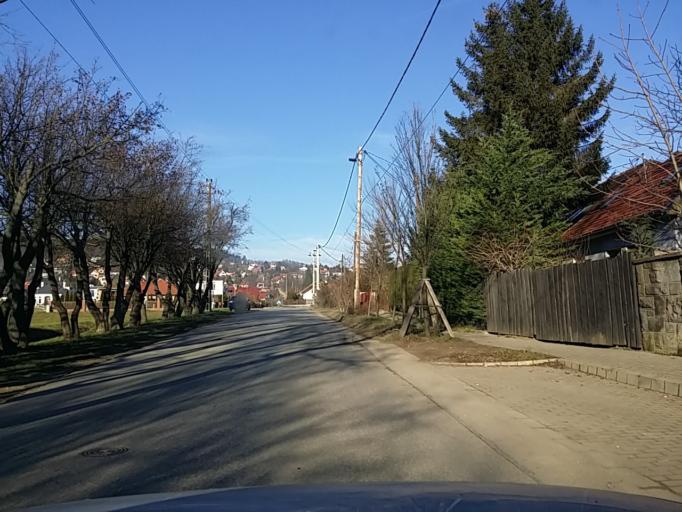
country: HU
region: Pest
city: Pilisszentivan
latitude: 47.5780
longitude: 18.8838
